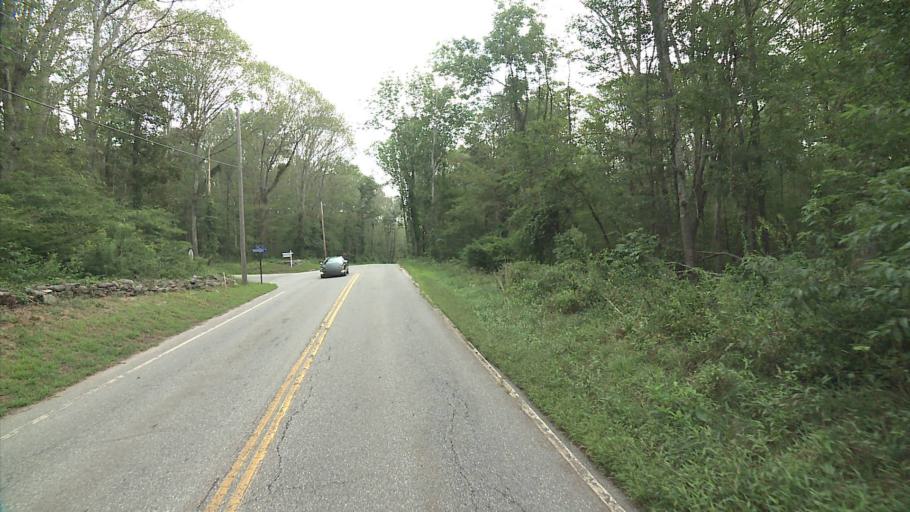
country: US
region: Connecticut
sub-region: New London County
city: Colchester
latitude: 41.4594
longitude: -72.3004
